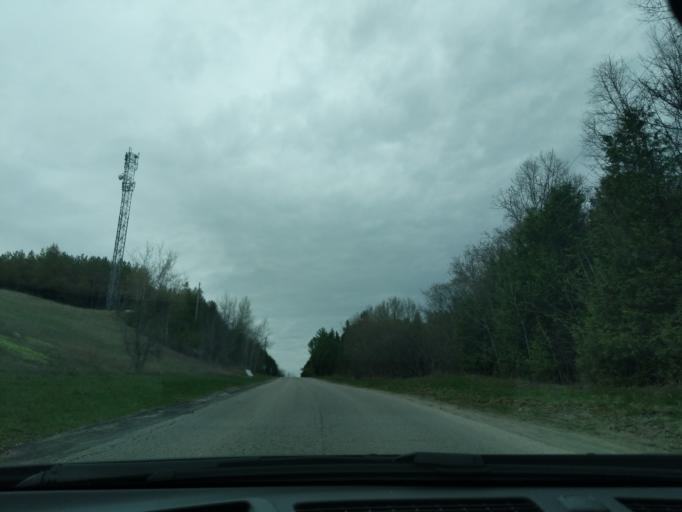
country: CA
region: Ontario
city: Orangeville
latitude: 44.0174
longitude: -79.9683
